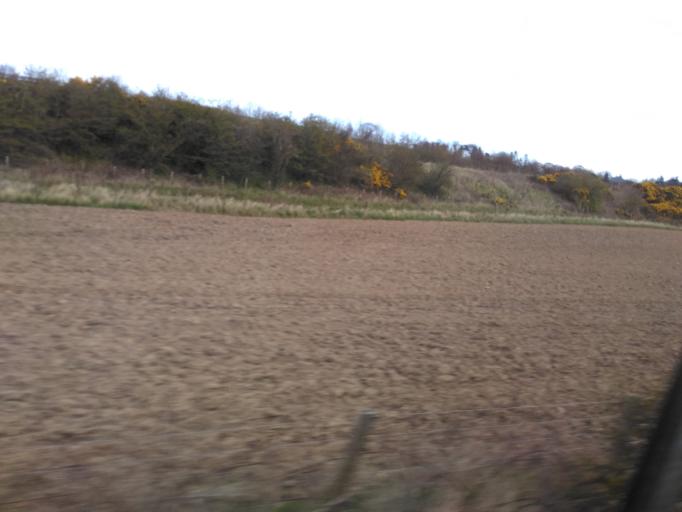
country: GB
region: Scotland
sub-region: The Scottish Borders
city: Chirnside
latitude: 55.8600
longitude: -2.2446
